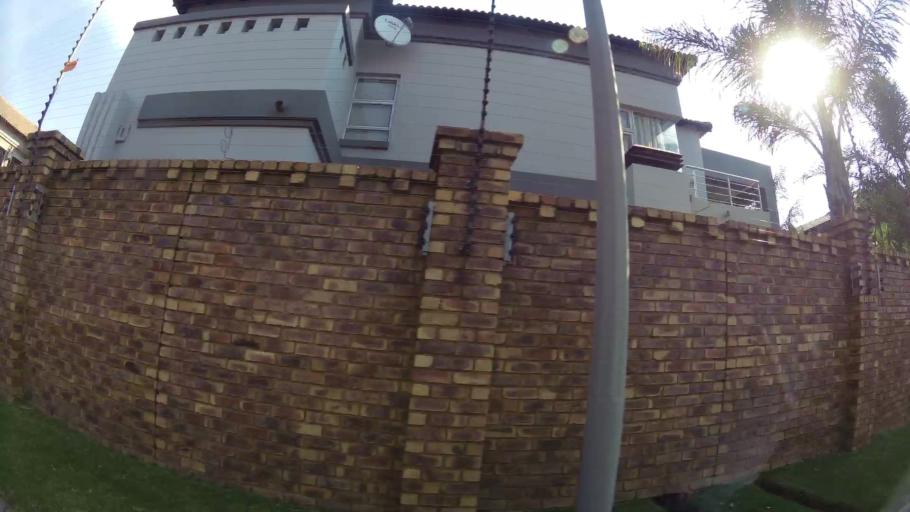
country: ZA
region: Gauteng
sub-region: Ekurhuleni Metropolitan Municipality
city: Boksburg
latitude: -26.1816
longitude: 28.2636
